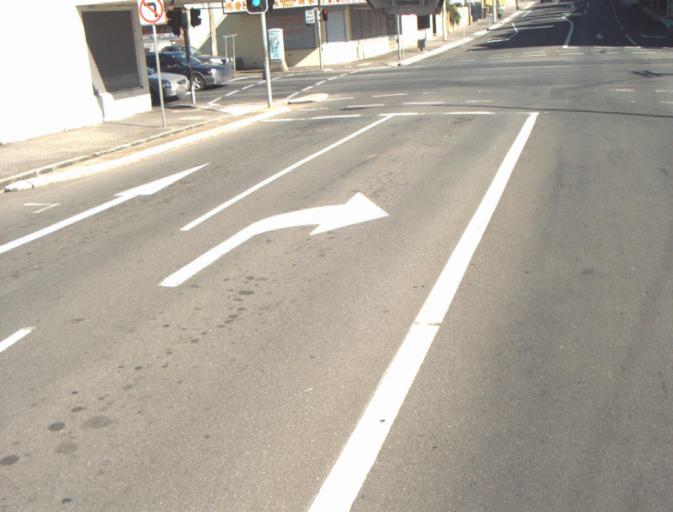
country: AU
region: Tasmania
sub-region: Launceston
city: Launceston
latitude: -41.4410
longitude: 147.1328
